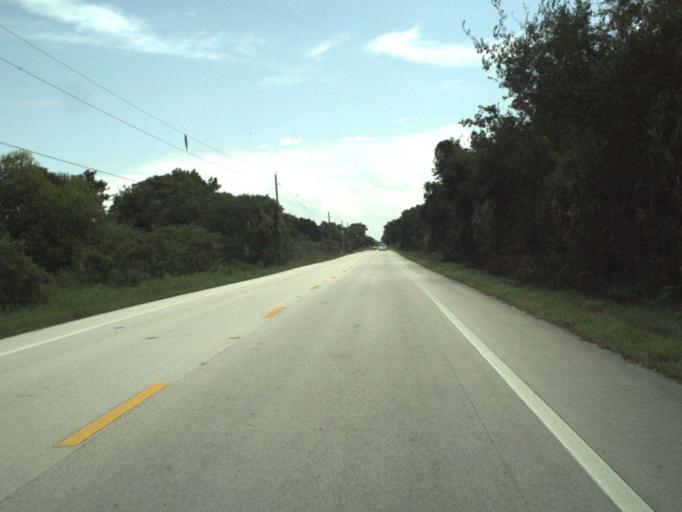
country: US
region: Florida
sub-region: Martin County
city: Indiantown
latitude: 27.0173
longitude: -80.6288
